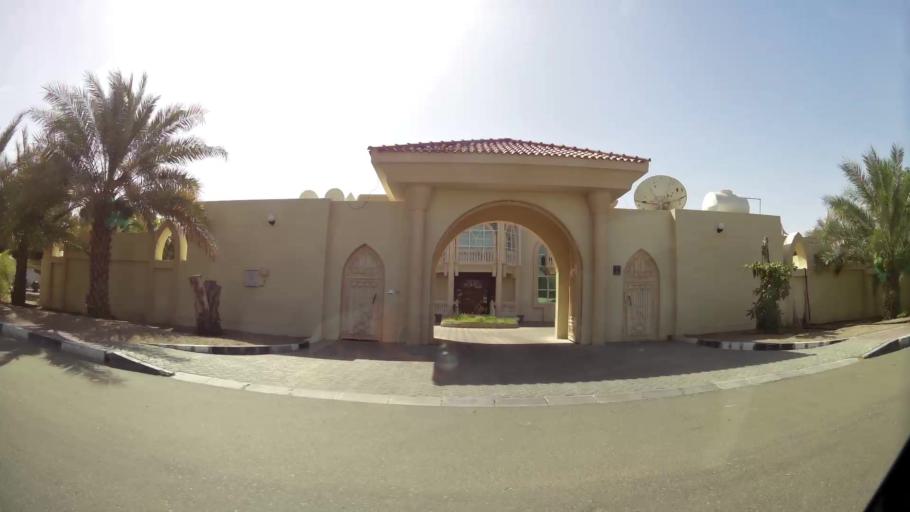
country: OM
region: Al Buraimi
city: Al Buraymi
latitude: 24.3102
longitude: 55.8043
